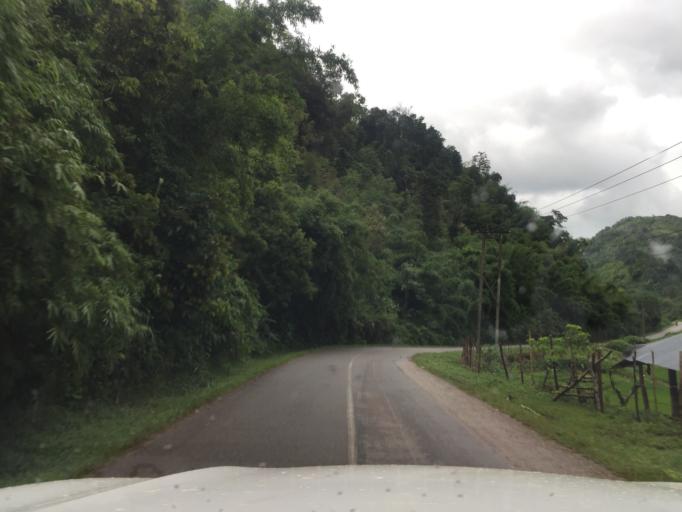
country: LA
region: Oudomxai
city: Muang La
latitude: 20.8226
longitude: 102.0965
